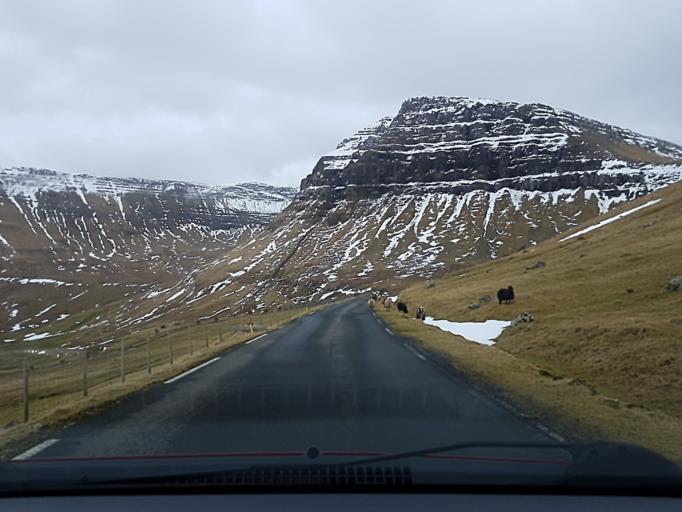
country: FO
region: Streymoy
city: Kollafjordhur
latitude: 62.0147
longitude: -6.9101
